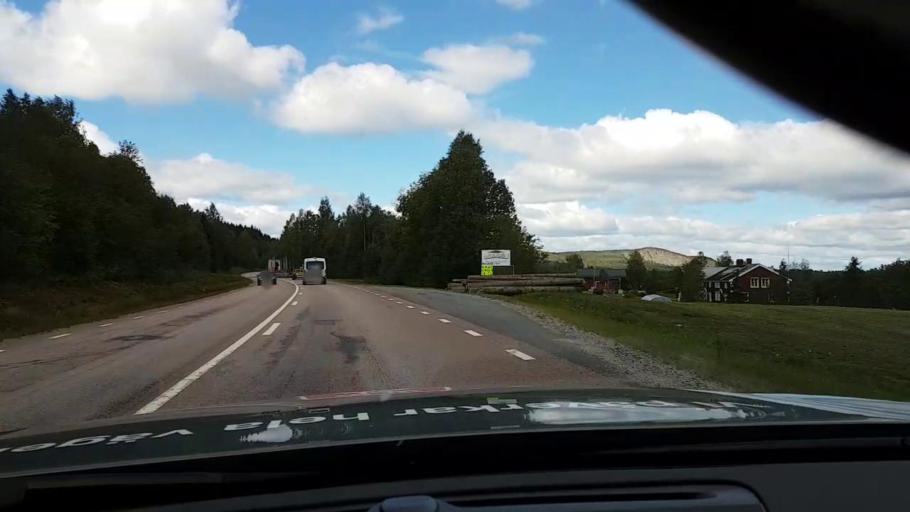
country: SE
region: Vaesternorrland
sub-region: OErnskoeldsviks Kommun
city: Bjasta
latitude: 63.3623
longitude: 18.4608
